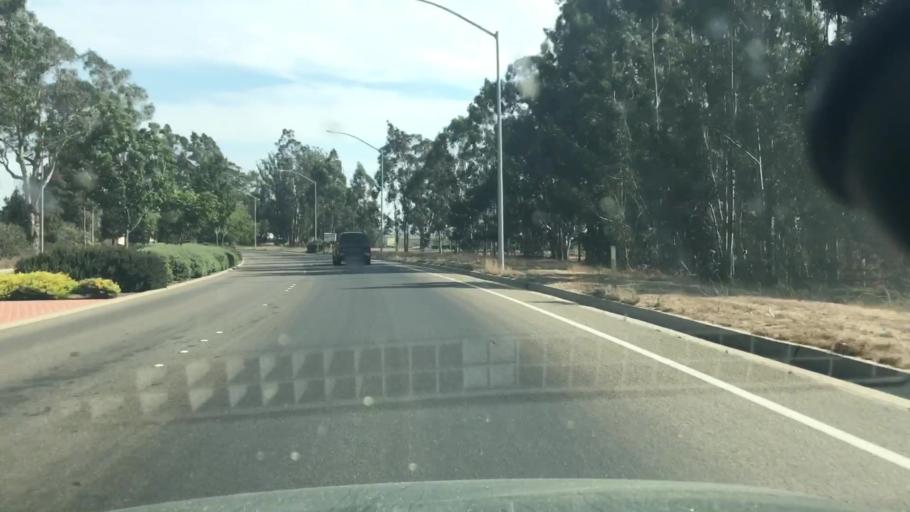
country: US
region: California
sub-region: Santa Barbara County
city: Orcutt
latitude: 34.9078
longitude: -120.4542
